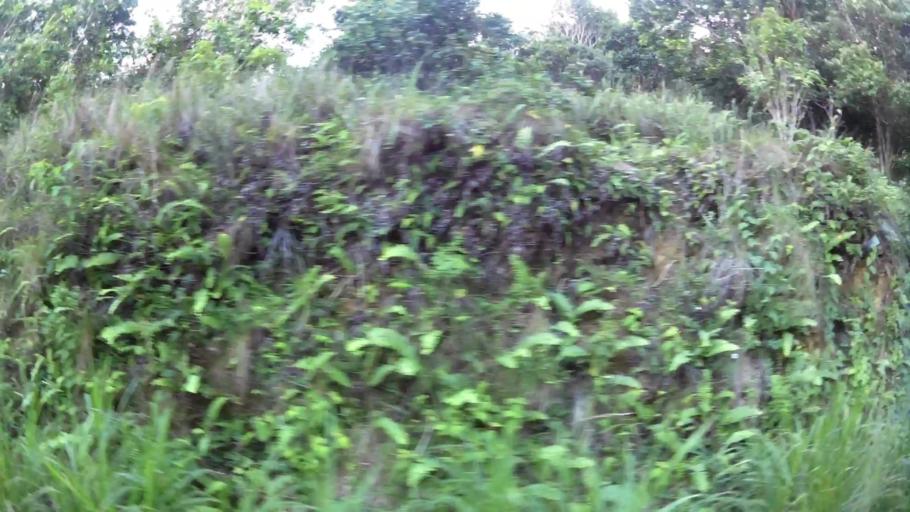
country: VG
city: Road Town
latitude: 18.4107
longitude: -64.6544
